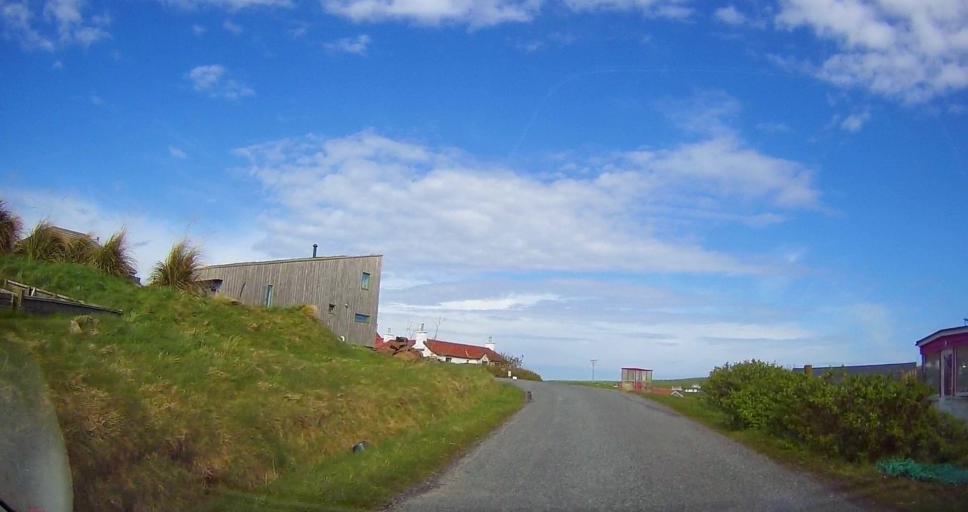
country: GB
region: Scotland
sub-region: Shetland Islands
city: Sandwick
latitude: 59.9751
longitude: -1.3200
